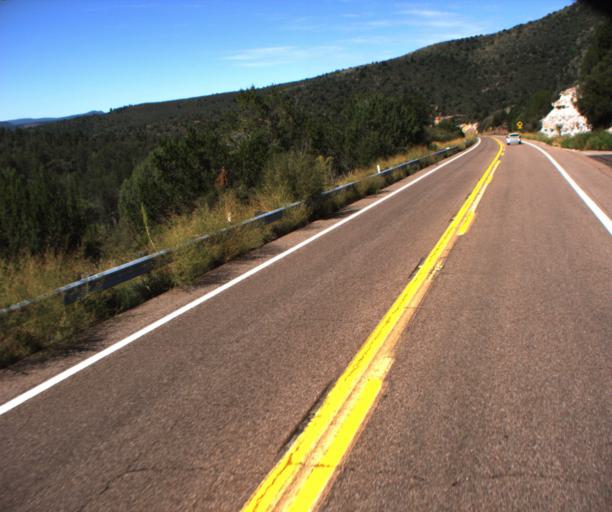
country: US
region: Arizona
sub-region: Navajo County
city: Cibecue
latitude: 33.8273
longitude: -110.4571
